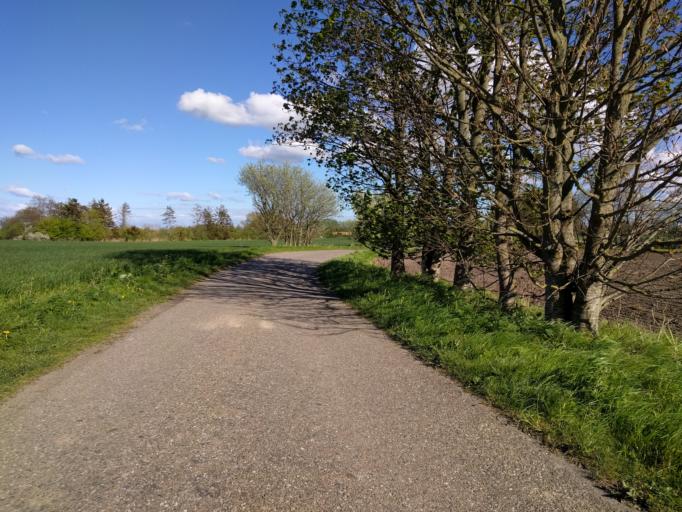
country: DK
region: South Denmark
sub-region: Kerteminde Kommune
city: Munkebo
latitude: 55.4547
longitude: 10.5150
